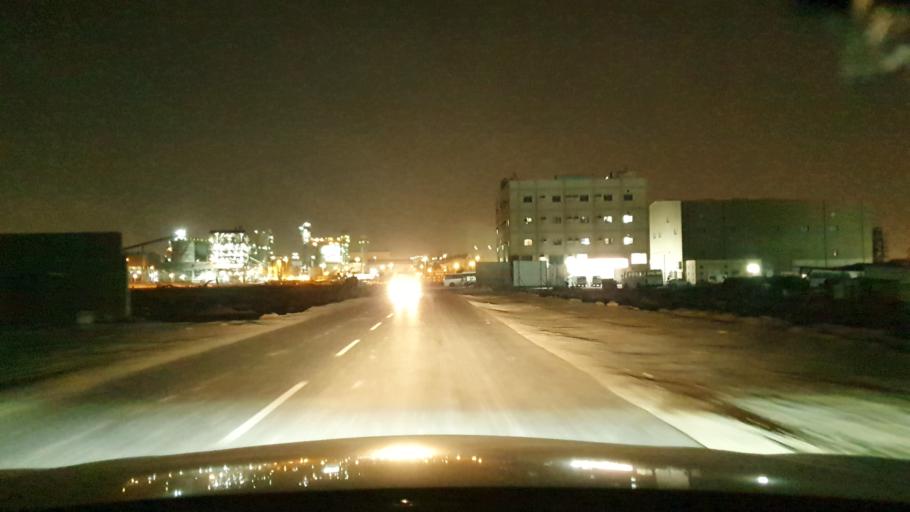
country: BH
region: Northern
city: Sitrah
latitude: 26.0945
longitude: 50.6128
